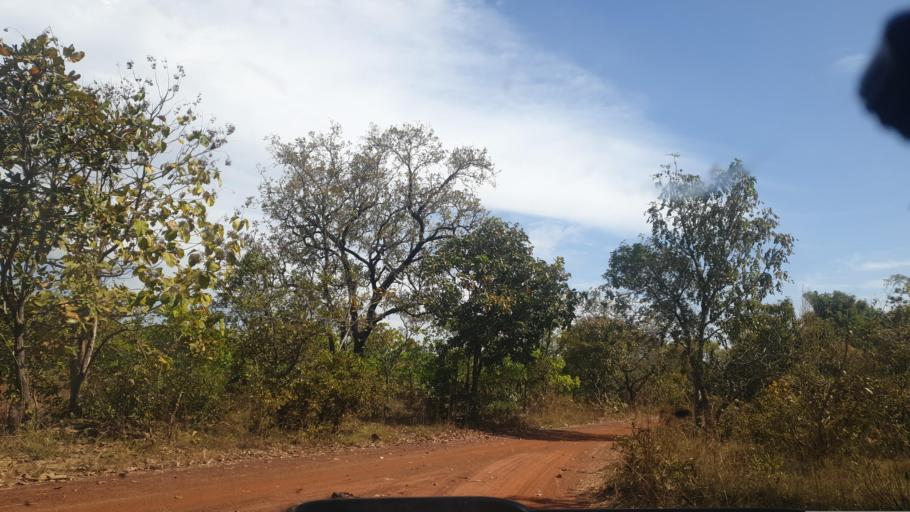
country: ML
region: Sikasso
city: Yanfolila
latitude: 10.4979
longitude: -7.9599
